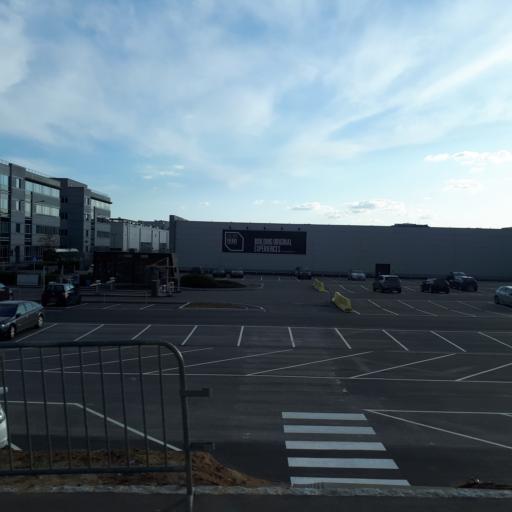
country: LU
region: Luxembourg
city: Kirchberg
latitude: 49.6358
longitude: 6.1748
